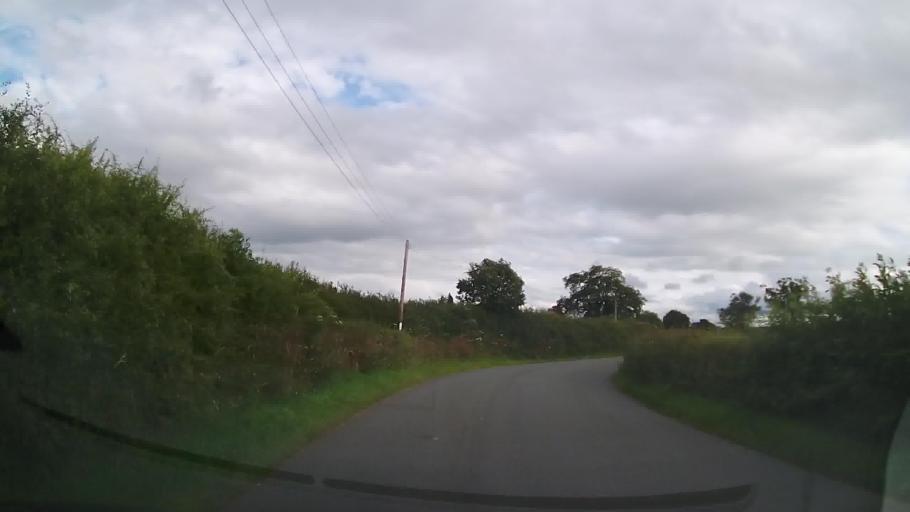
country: GB
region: England
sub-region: Shropshire
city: Wem
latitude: 52.8993
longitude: -2.7638
